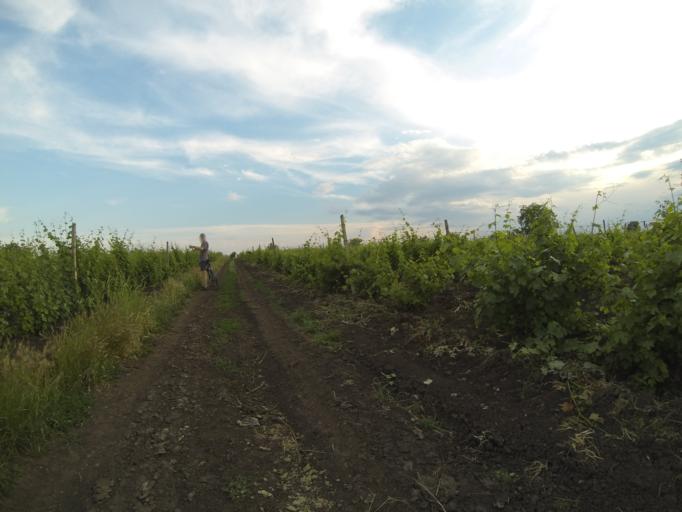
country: RO
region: Dolj
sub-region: Comuna Ceratu
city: Ceratu
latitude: 44.1134
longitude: 23.6824
